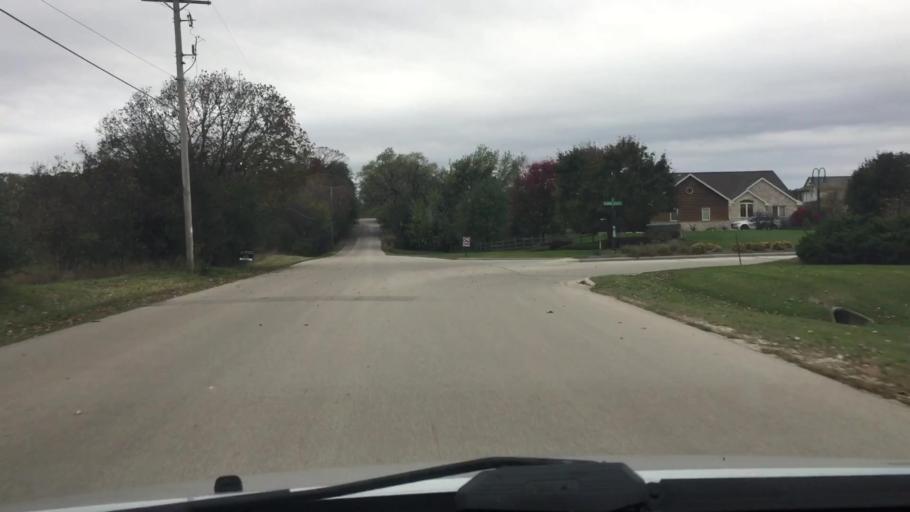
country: US
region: Wisconsin
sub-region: Waukesha County
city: North Prairie
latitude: 42.9304
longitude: -88.4276
